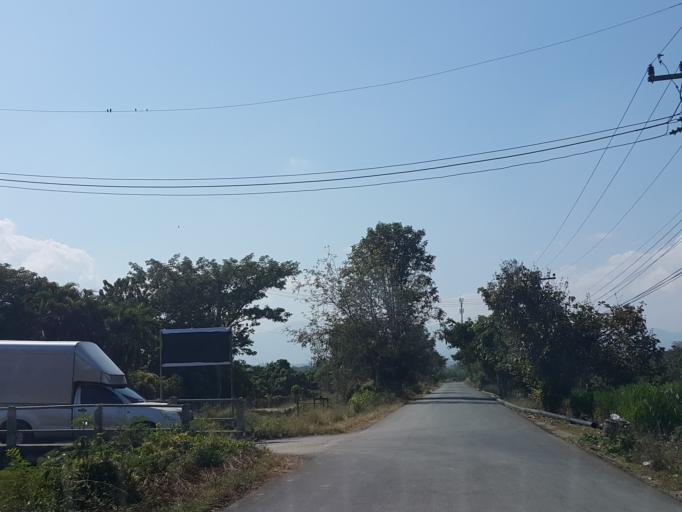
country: TH
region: Chiang Mai
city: Mae Taeng
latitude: 19.0376
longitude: 98.9739
